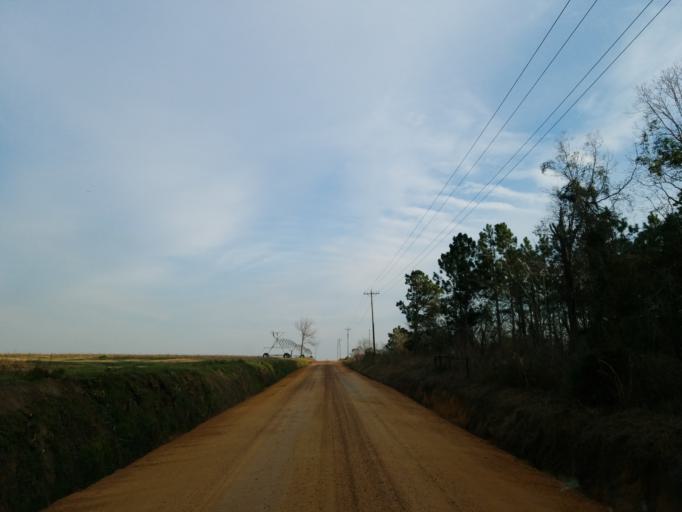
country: US
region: Georgia
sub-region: Tift County
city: Omega
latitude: 31.3684
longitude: -83.6114
